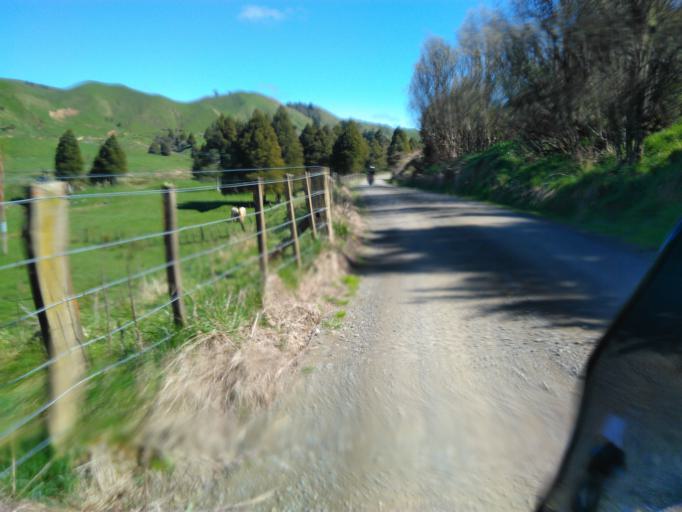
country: NZ
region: Bay of Plenty
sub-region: Opotiki District
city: Opotiki
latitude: -38.2989
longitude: 177.5567
